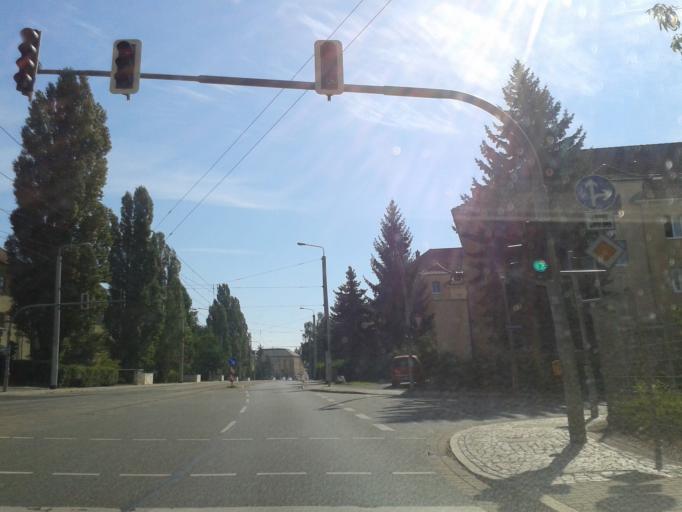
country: DE
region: Saxony
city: Dresden
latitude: 51.0281
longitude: 13.7961
